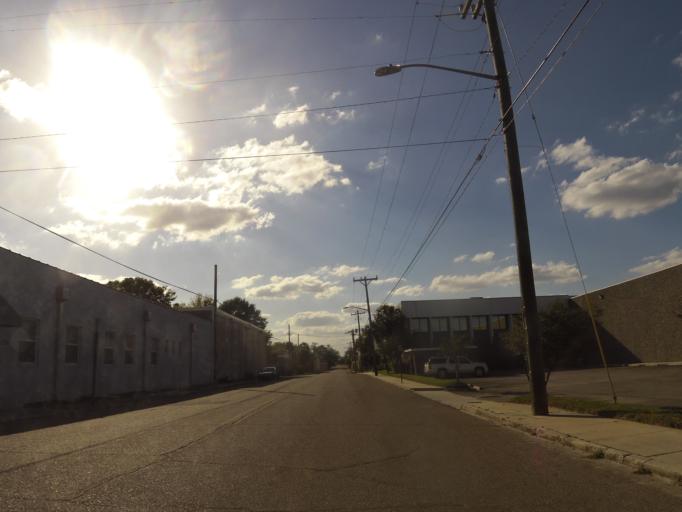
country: US
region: Florida
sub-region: Duval County
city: Jacksonville
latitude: 30.3300
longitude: -81.6836
